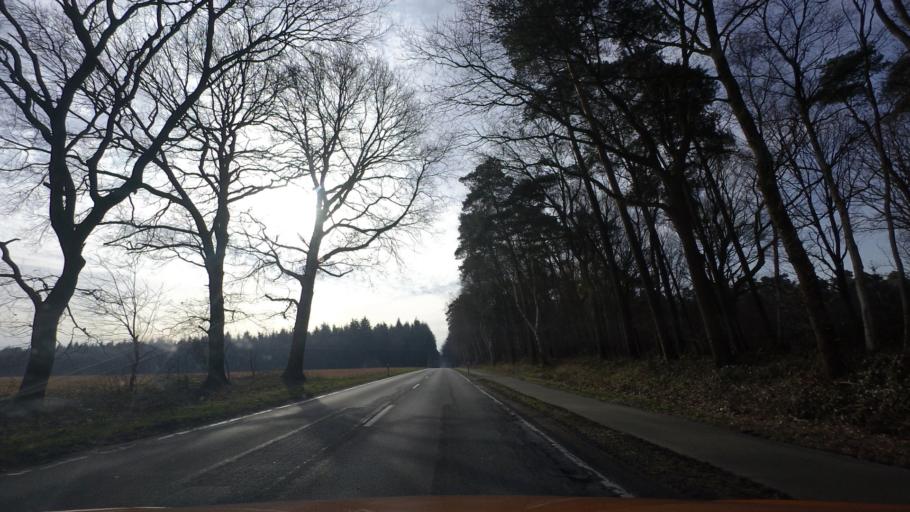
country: DE
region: Lower Saxony
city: Hatten
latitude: 53.0063
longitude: 8.3773
